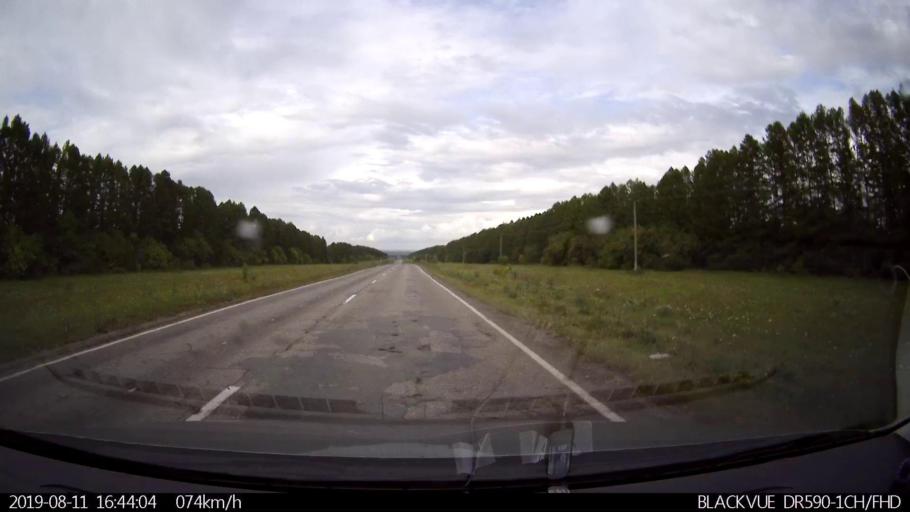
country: RU
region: Ulyanovsk
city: Mayna
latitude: 54.1756
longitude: 47.6778
